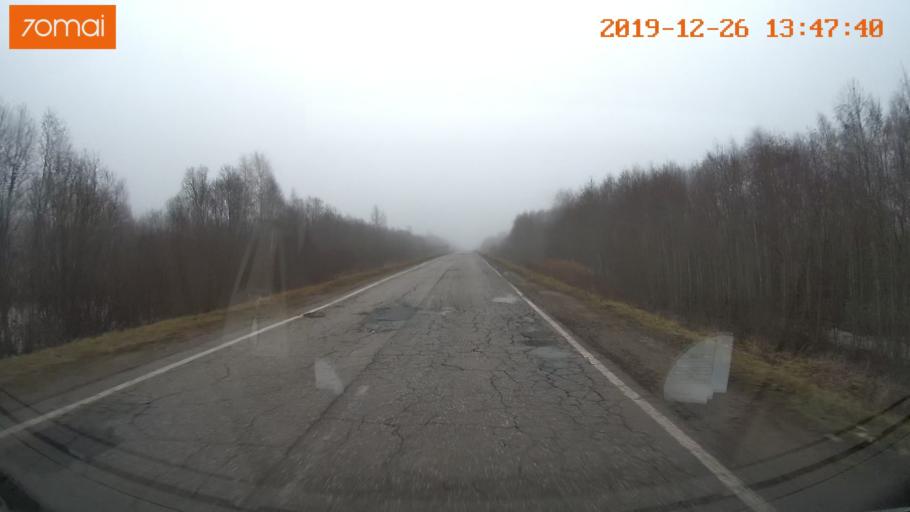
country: RU
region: Vologda
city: Sheksna
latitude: 58.6831
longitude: 38.5368
